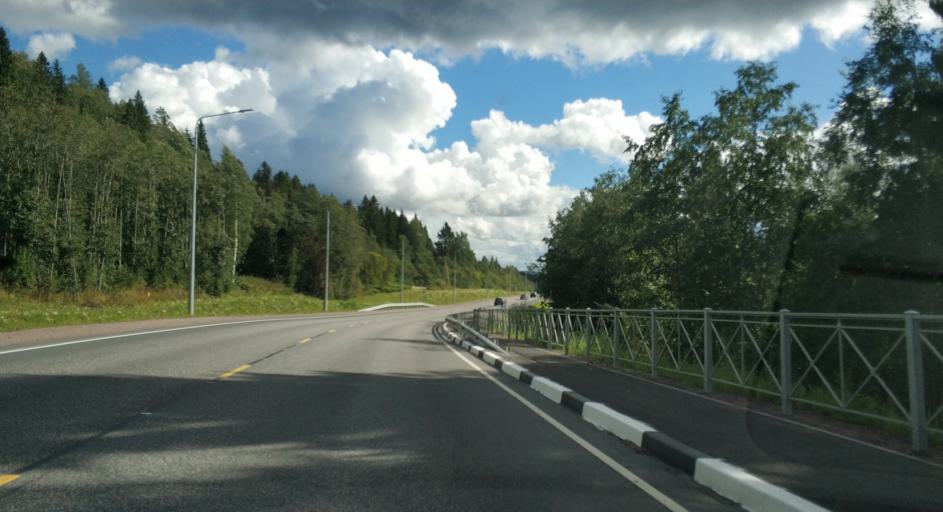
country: RU
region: Republic of Karelia
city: Ruskeala
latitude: 61.9245
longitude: 30.6036
